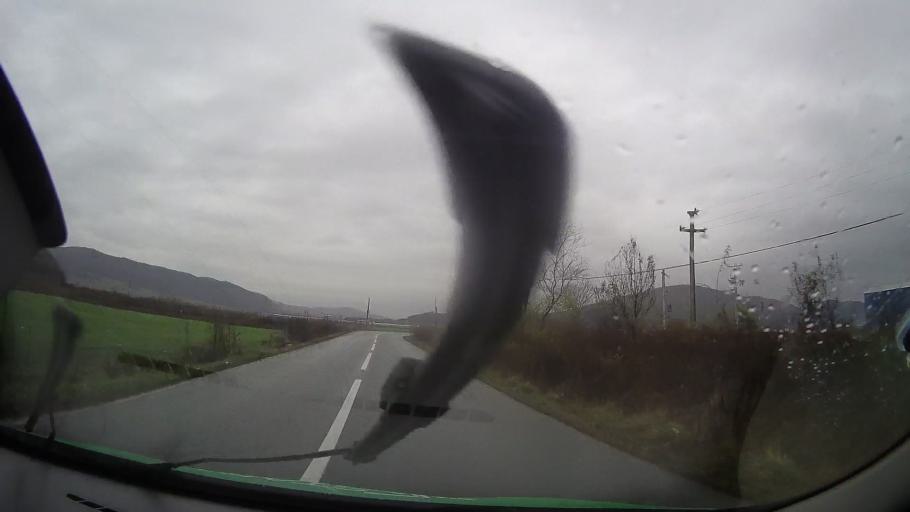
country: RO
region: Bistrita-Nasaud
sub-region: Municipiul Bistrita
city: Viisoara
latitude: 47.0578
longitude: 24.4369
